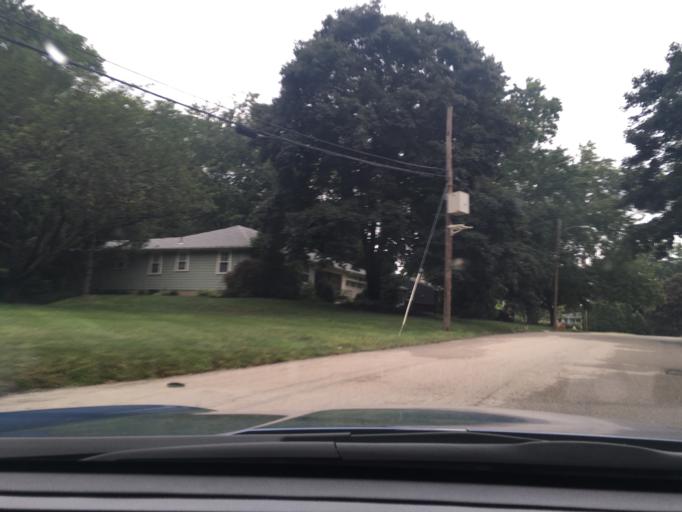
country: US
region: Rhode Island
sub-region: Kent County
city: East Greenwich
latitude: 41.6660
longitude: -71.4592
